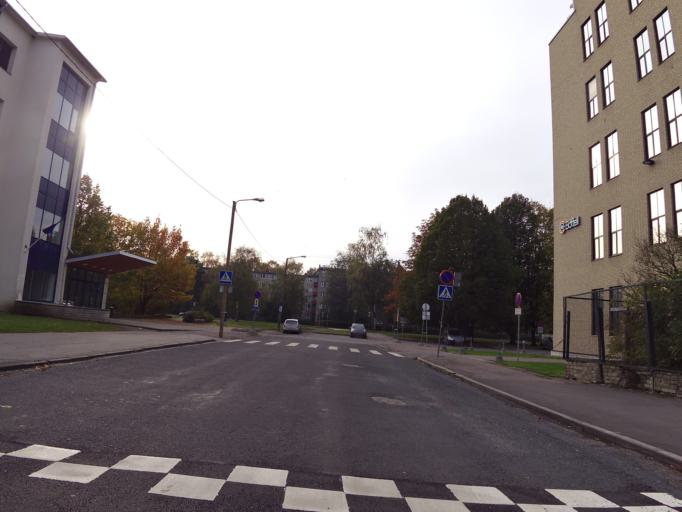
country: EE
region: Harju
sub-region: Tallinna linn
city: Tallinn
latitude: 59.4348
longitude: 24.7148
